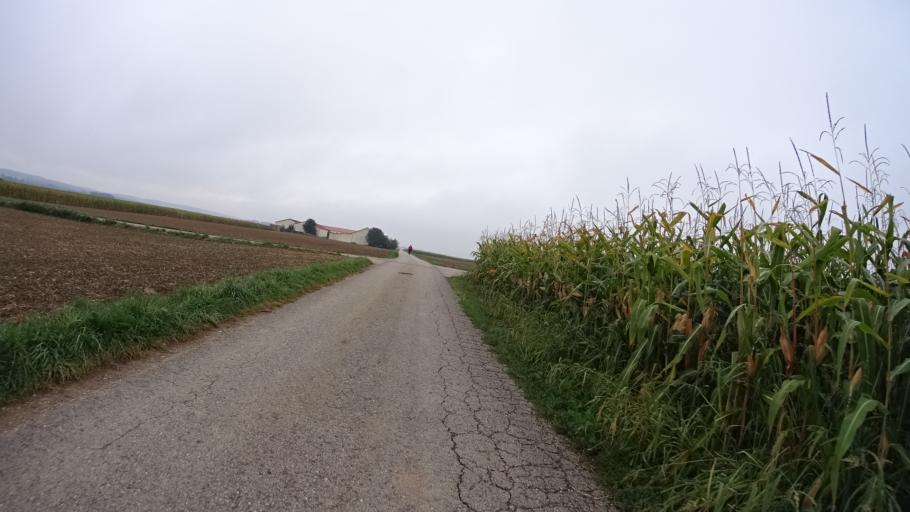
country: DE
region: Bavaria
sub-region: Upper Bavaria
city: Gaimersheim
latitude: 48.8168
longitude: 11.3782
